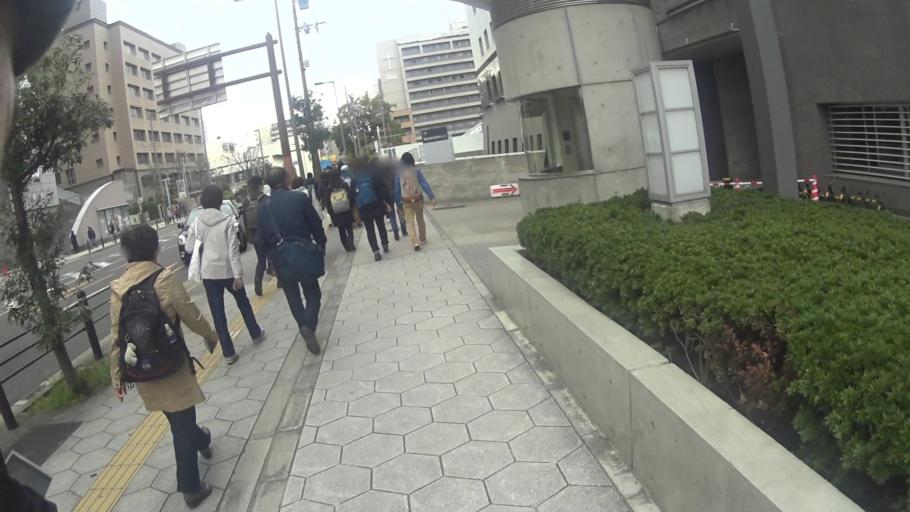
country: JP
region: Osaka
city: Osaka-shi
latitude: 34.6836
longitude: 135.5211
